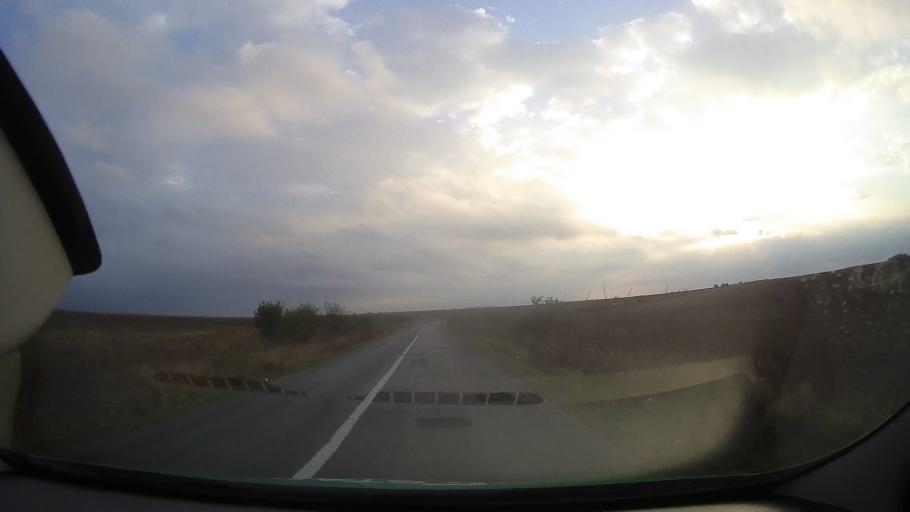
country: RO
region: Constanta
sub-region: Comuna Adamclisi
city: Adamclisi
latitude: 44.0194
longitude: 27.9060
